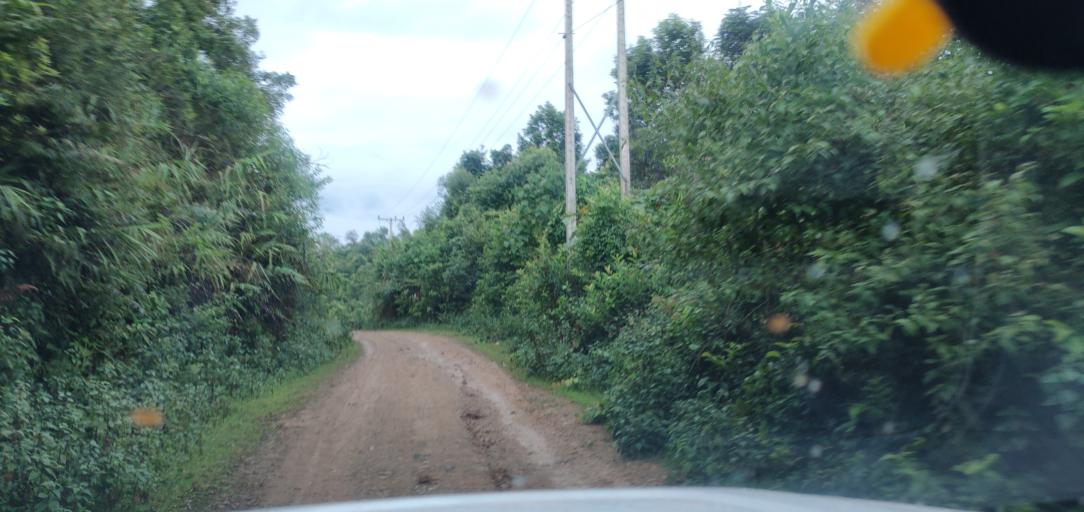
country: LA
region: Phongsali
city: Phongsali
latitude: 21.4343
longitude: 102.2615
